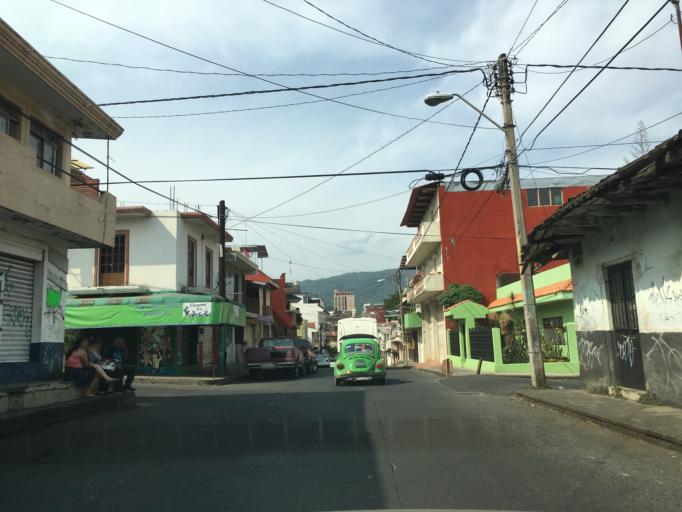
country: MX
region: Michoacan
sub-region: Uruapan
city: Uruapan
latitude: 19.4133
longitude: -102.0641
